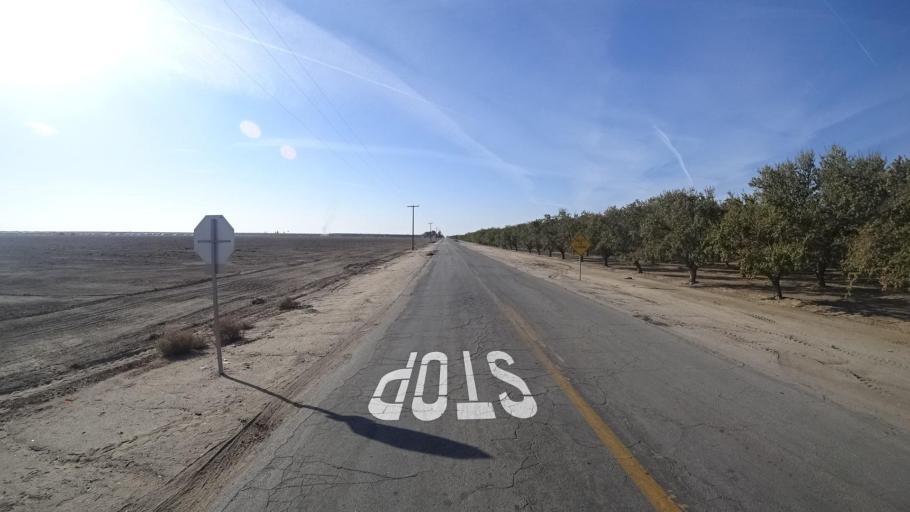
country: US
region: California
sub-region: Kern County
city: McFarland
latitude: 35.7033
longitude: -119.2410
